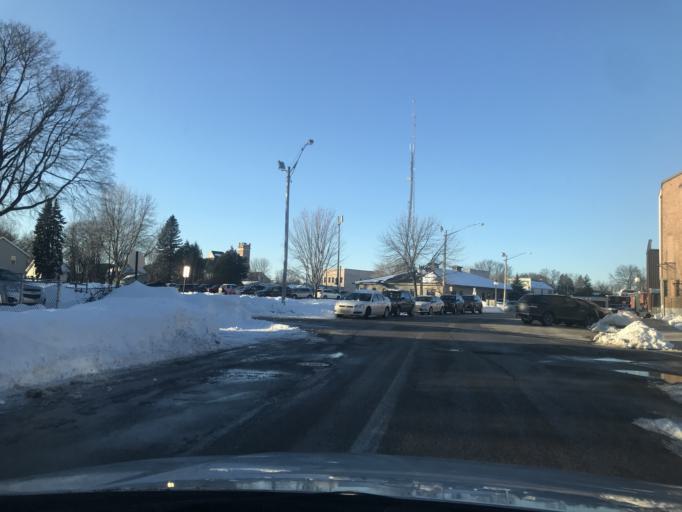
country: US
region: Michigan
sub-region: Menominee County
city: Menominee
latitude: 45.1061
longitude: -87.6056
